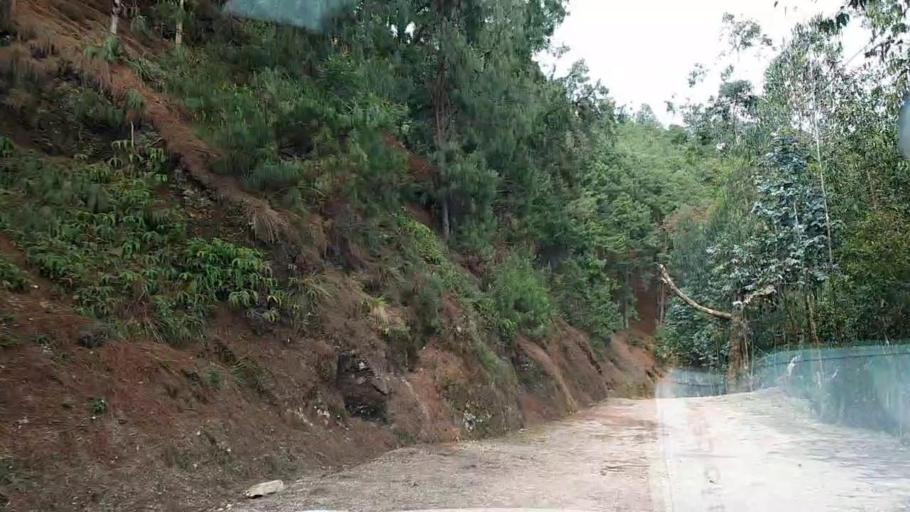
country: RW
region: Southern Province
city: Nzega
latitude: -2.4092
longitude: 29.4557
